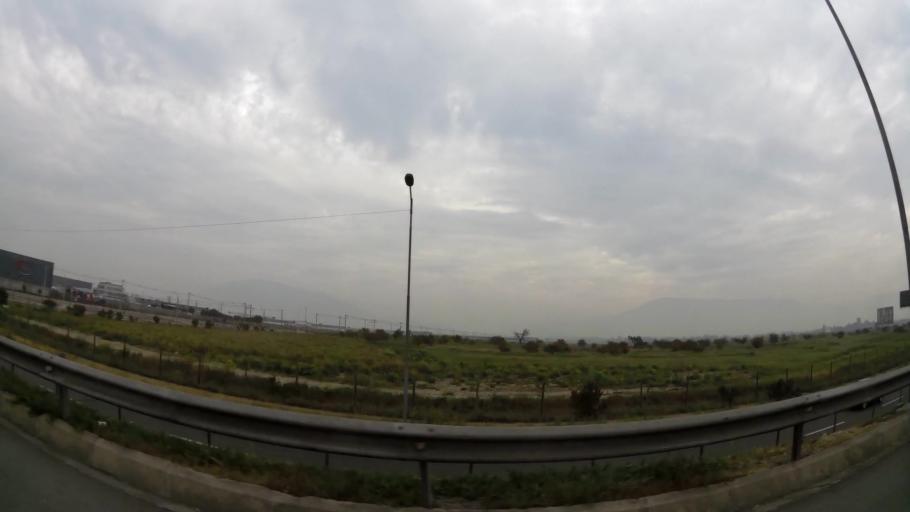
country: CL
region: Santiago Metropolitan
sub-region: Provincia de Santiago
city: Lo Prado
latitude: -33.4246
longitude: -70.7854
